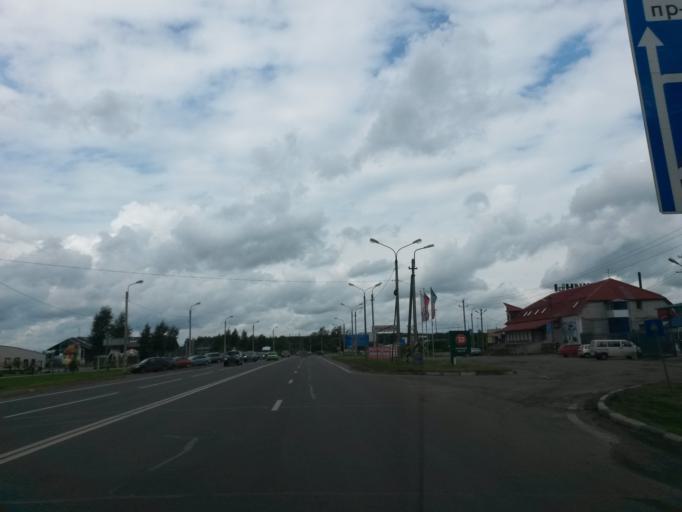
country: RU
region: Jaroslavl
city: Yaroslavl
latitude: 57.6770
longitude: 39.9032
